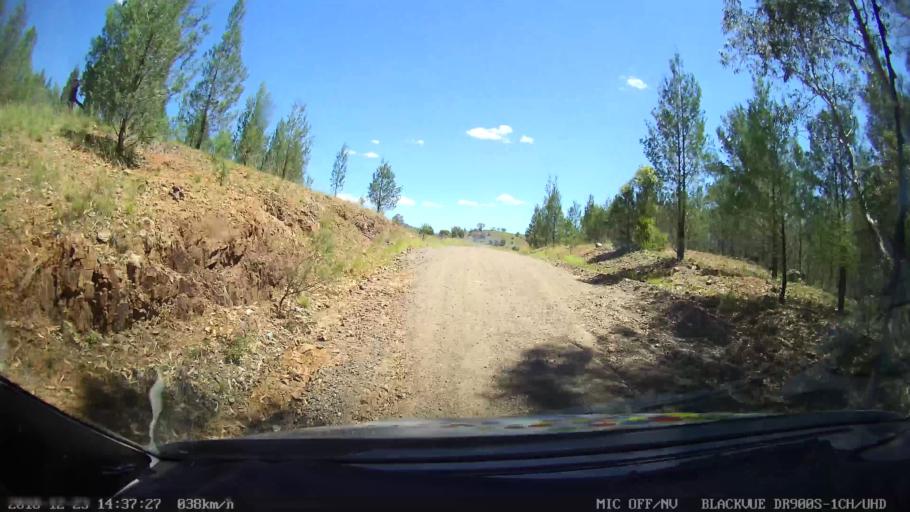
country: AU
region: New South Wales
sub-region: Tamworth Municipality
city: Manilla
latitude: -30.6157
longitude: 150.9073
